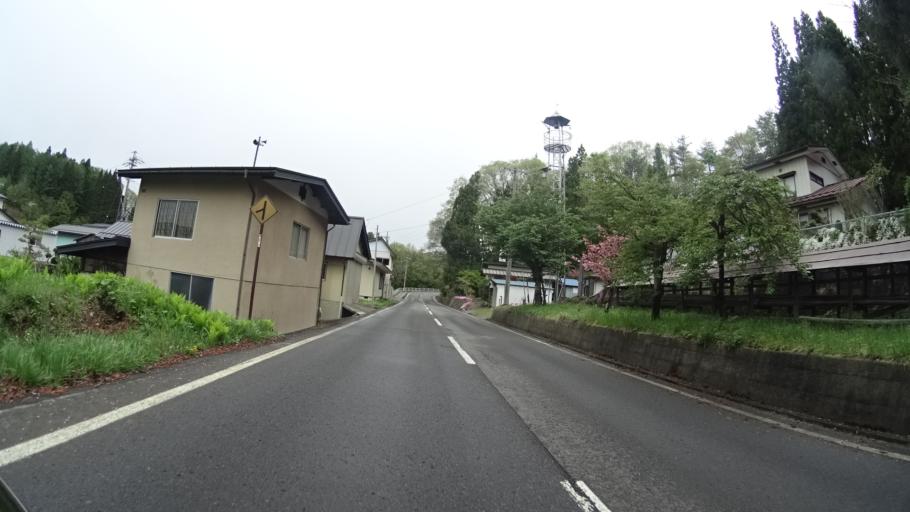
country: JP
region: Nagano
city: Nagano-shi
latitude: 36.7602
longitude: 138.1984
